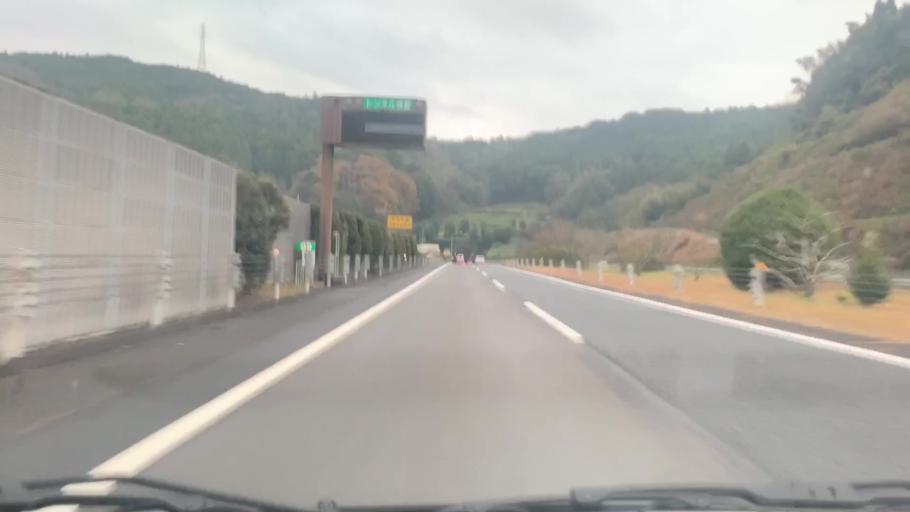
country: JP
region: Nagasaki
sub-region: Isahaya-shi
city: Isahaya
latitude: 32.8760
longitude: 129.9975
